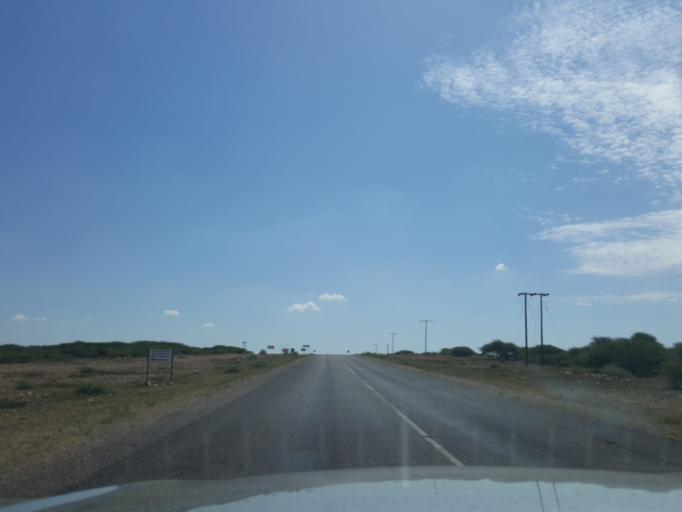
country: BW
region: Kweneng
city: Letlhakeng
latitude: -24.1178
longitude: 25.0513
